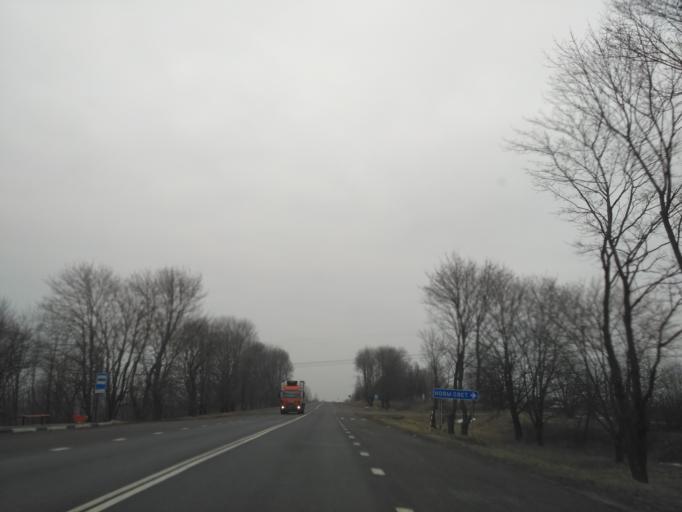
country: BY
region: Brest
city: Baranovichi
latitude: 53.1795
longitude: 26.0618
